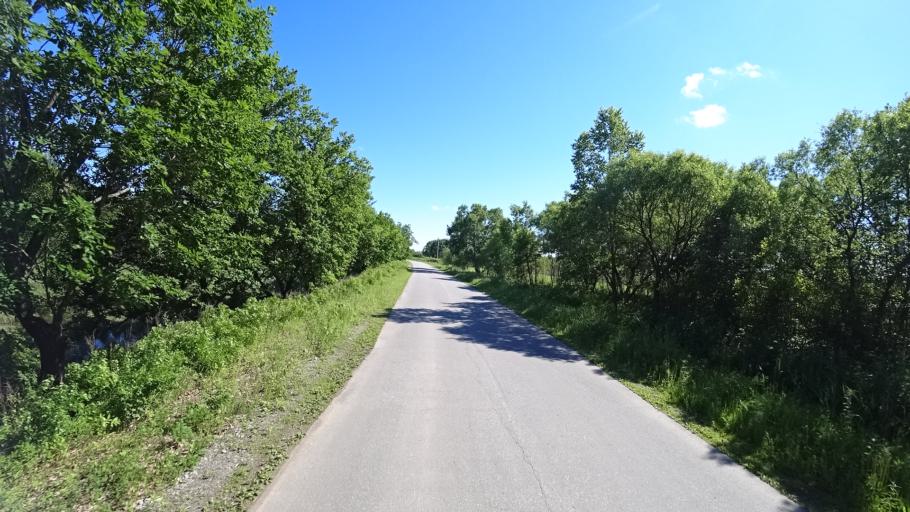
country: RU
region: Khabarovsk Krai
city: Khor
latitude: 47.8930
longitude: 135.0226
